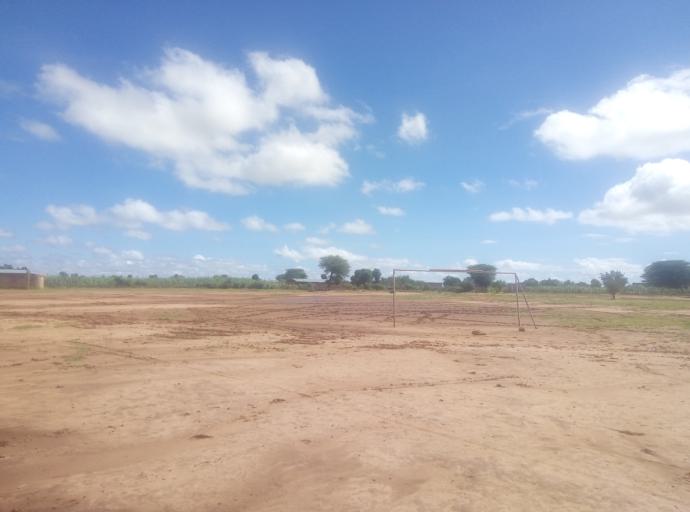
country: ML
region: Kayes
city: Yelimane
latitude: 15.1338
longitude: -10.7248
